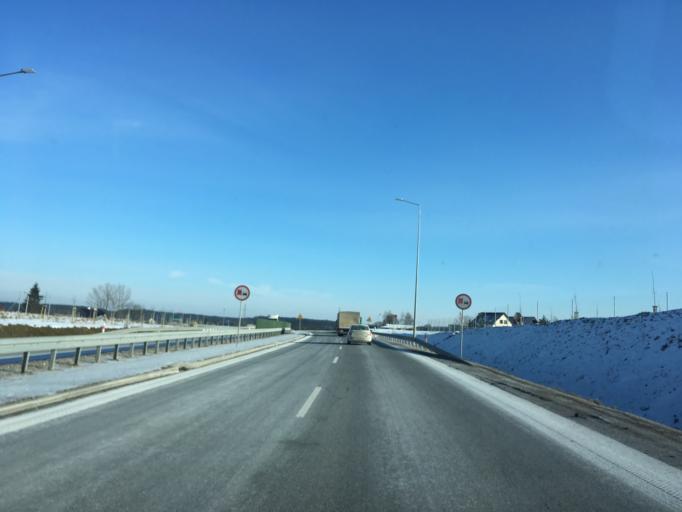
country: PL
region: Pomeranian Voivodeship
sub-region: Powiat koscierski
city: Koscierzyna
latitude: 54.1084
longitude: 17.9605
